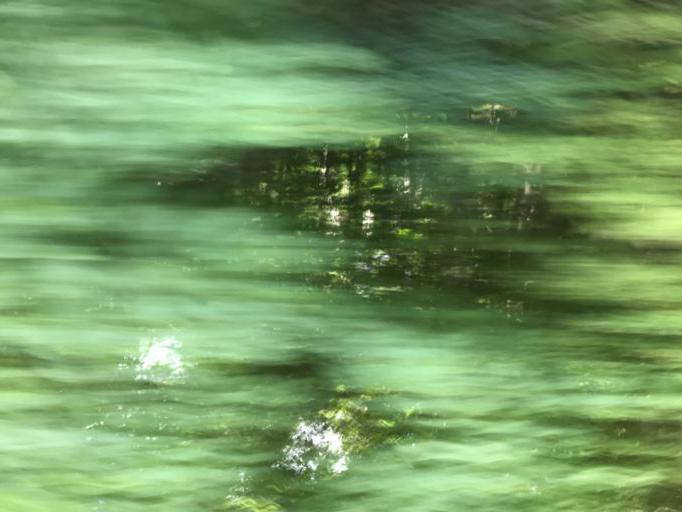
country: DE
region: Lower Saxony
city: Bad Harzburg
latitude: 51.8955
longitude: 10.6074
